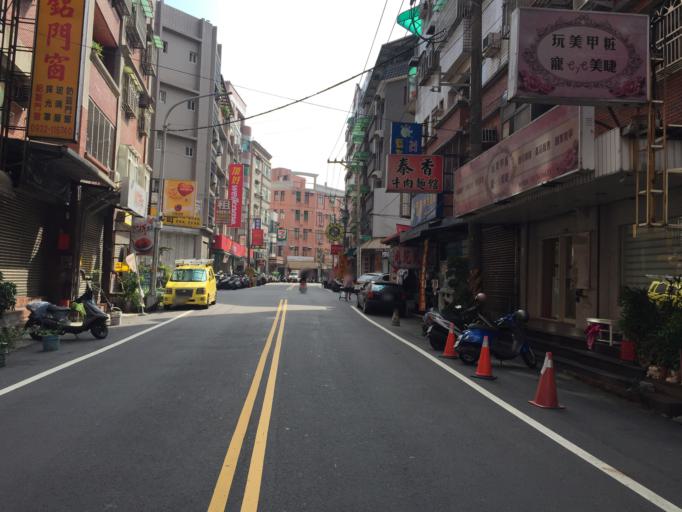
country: TW
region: Taiwan
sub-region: Hsinchu
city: Hsinchu
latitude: 24.7950
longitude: 120.9616
